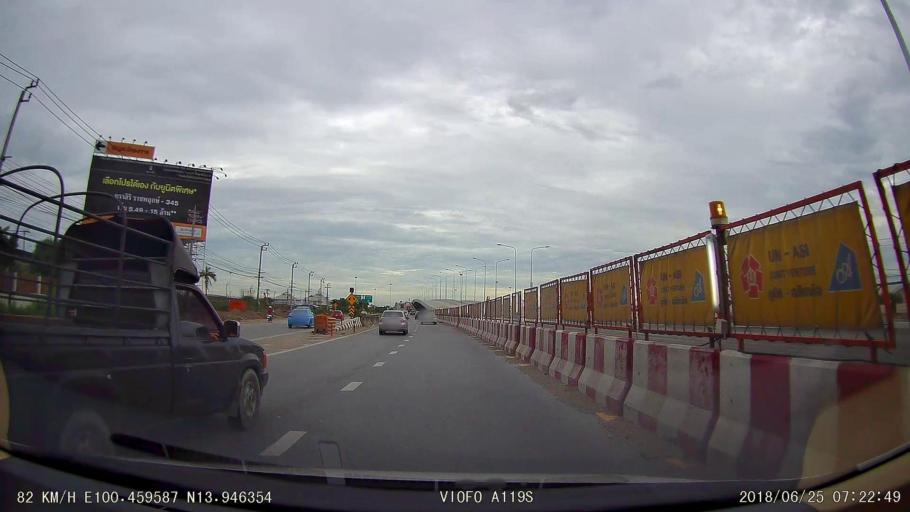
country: TH
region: Nonthaburi
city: Bang Bua Thong
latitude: 13.9462
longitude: 100.4594
